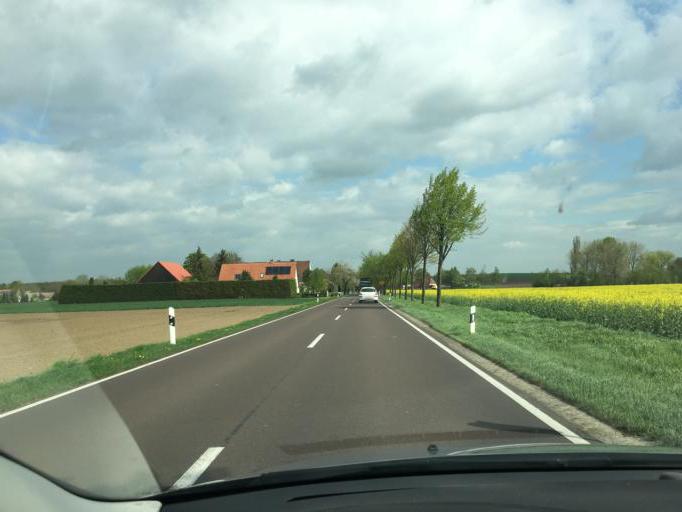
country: DE
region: Saxony-Anhalt
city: Giersleben
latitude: 51.7324
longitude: 11.5911
